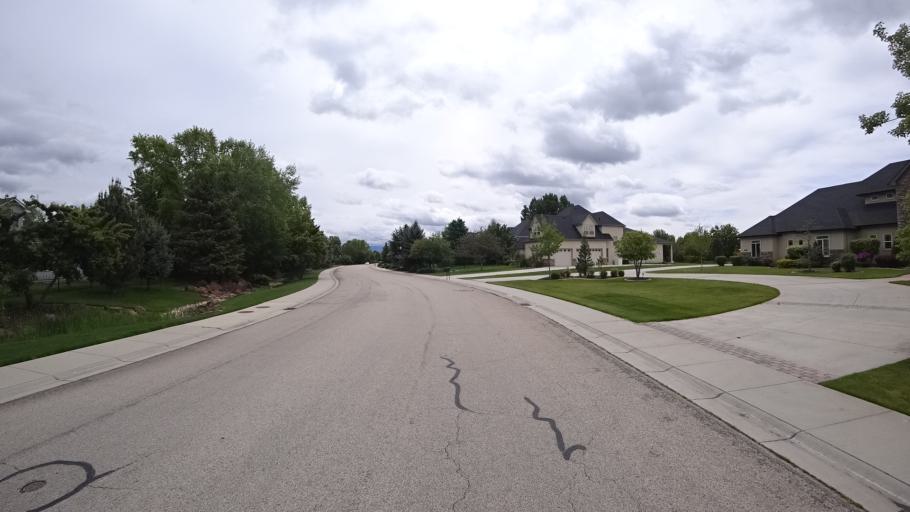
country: US
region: Idaho
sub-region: Ada County
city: Eagle
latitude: 43.6765
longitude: -116.3125
